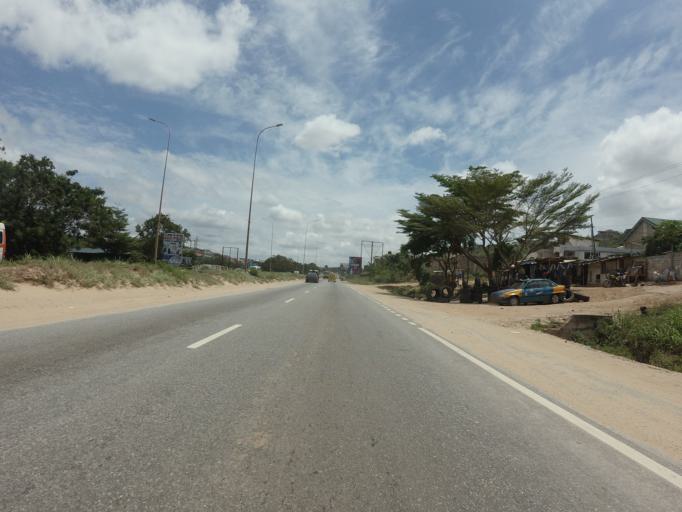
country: GH
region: Central
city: Kasoa
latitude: 5.5510
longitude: -0.3700
